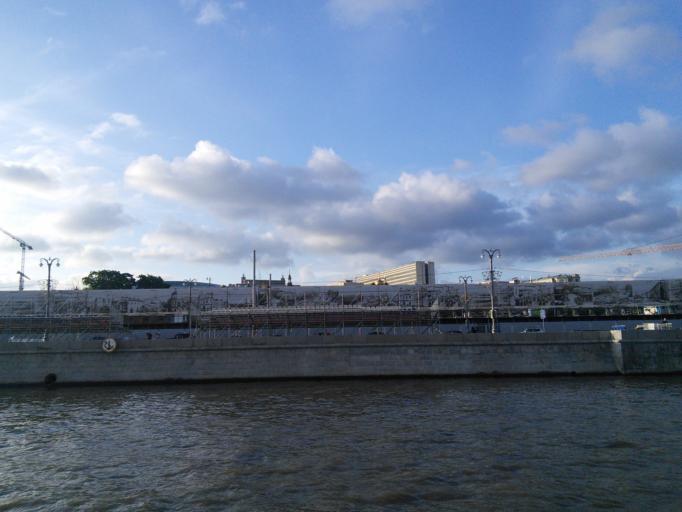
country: RU
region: Moscow
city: Moscow
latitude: 55.7492
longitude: 37.6279
